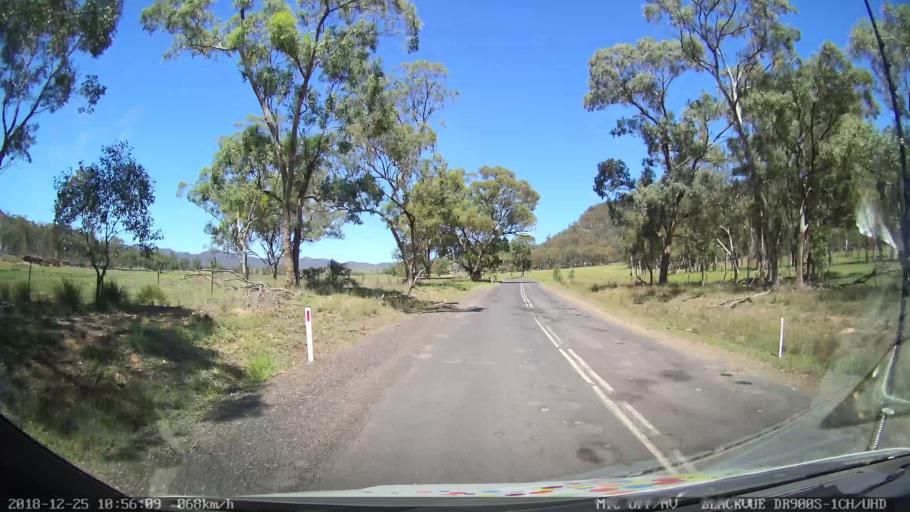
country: AU
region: New South Wales
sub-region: Upper Hunter Shire
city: Merriwa
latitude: -32.4001
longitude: 150.2659
